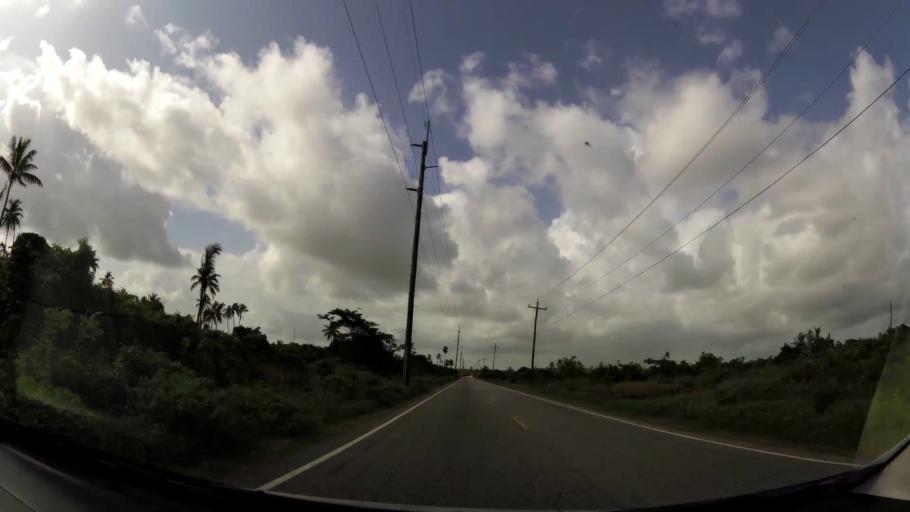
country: GY
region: Demerara-Mahaica
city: Mahaica Village
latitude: 6.6890
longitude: -57.9290
